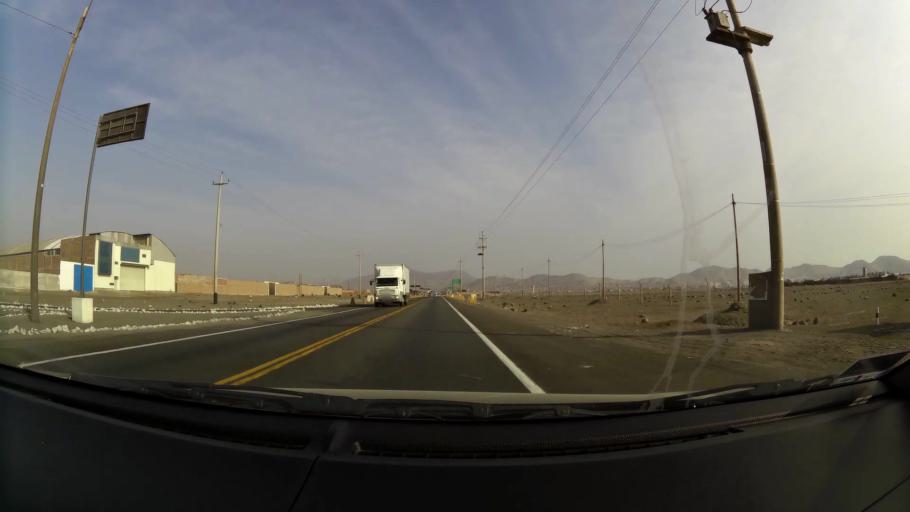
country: PE
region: Lima
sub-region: Lima
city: Santa Rosa
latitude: -11.7501
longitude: -77.1633
